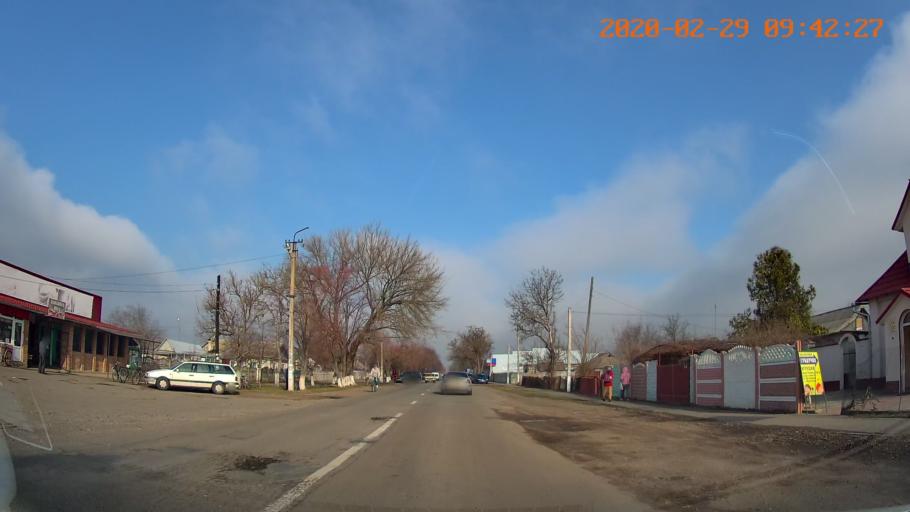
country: MD
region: Telenesti
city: Crasnoe
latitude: 46.6406
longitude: 29.8242
